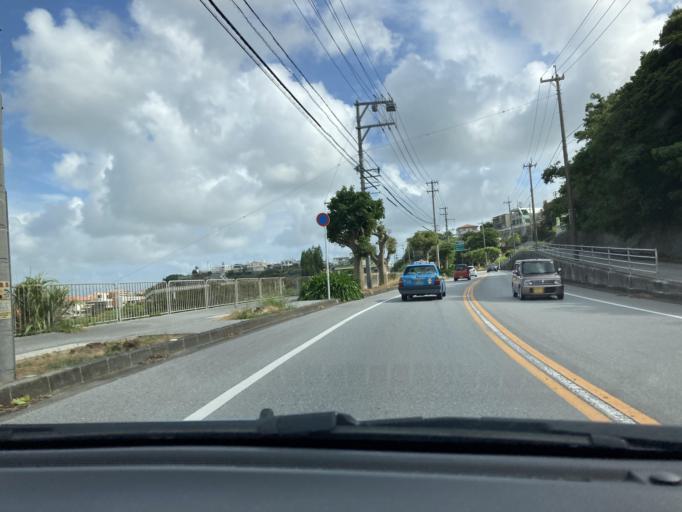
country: JP
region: Okinawa
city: Tomigusuku
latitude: 26.1743
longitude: 127.6891
